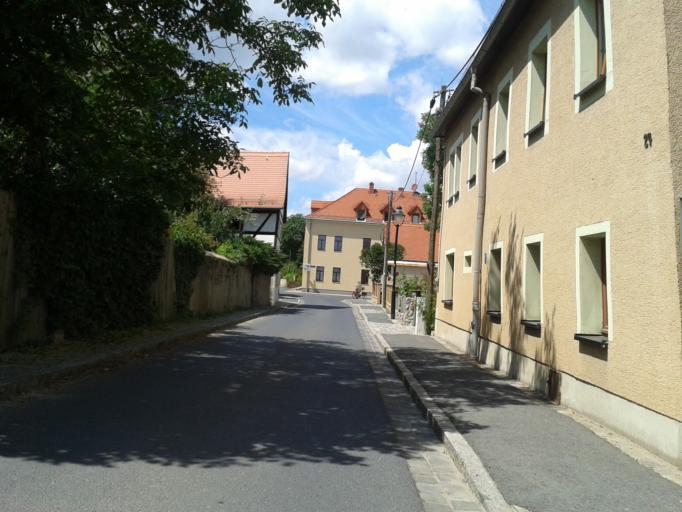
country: DE
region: Saxony
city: Radebeul
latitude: 51.0836
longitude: 13.6731
